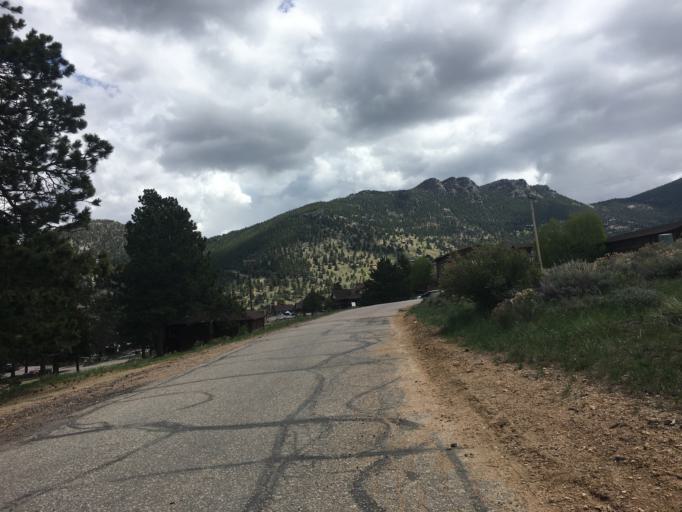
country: US
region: Colorado
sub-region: Larimer County
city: Estes Park
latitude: 40.3403
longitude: -105.5776
